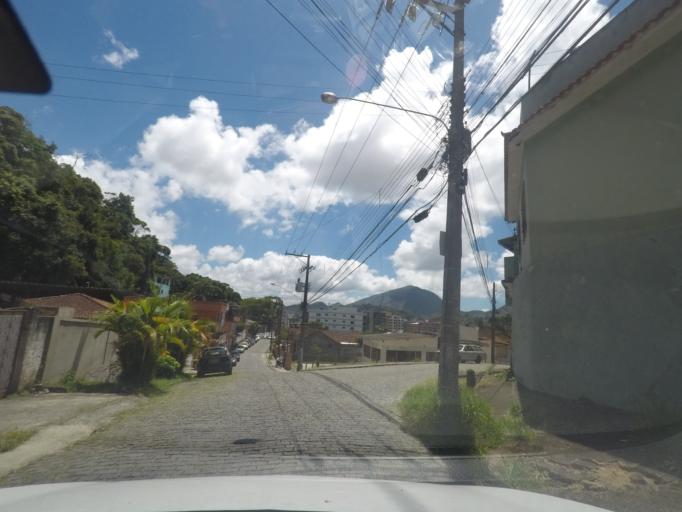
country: BR
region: Rio de Janeiro
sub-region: Teresopolis
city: Teresopolis
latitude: -22.4223
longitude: -42.9834
